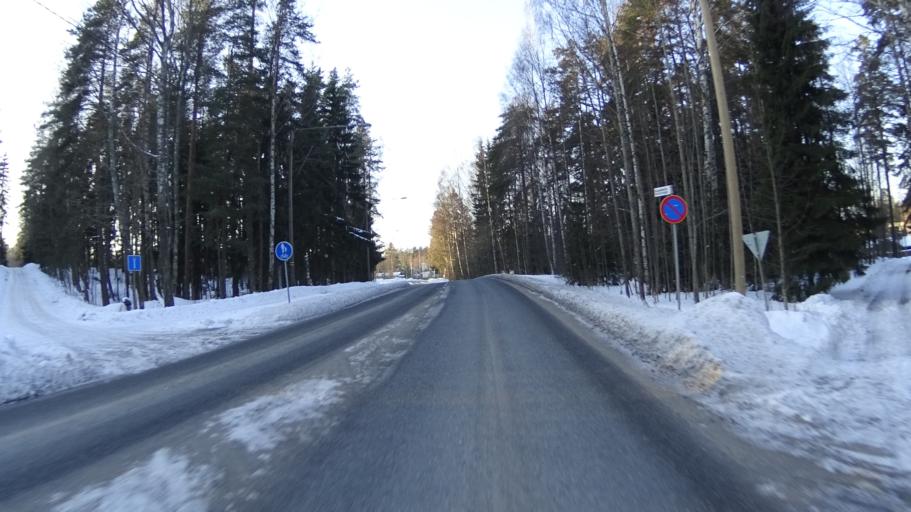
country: FI
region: Uusimaa
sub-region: Helsinki
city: Vantaa
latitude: 60.2597
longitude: 25.1003
